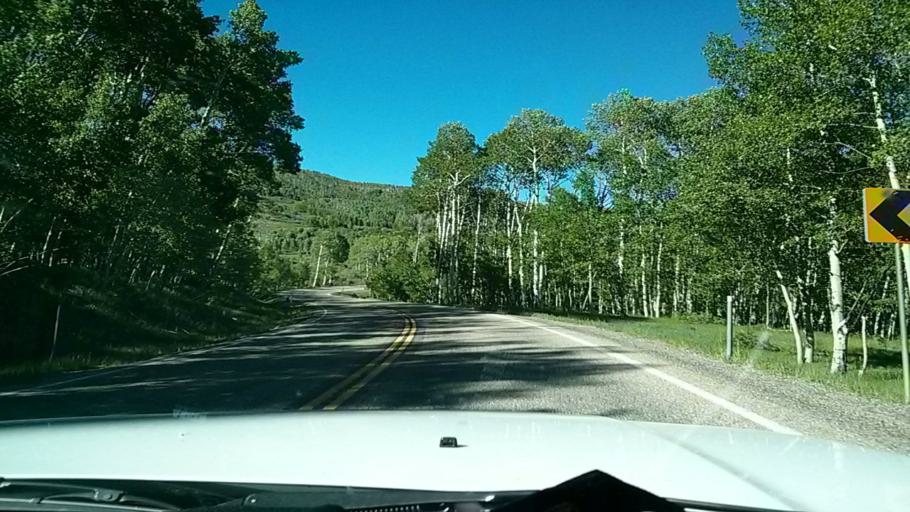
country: US
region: Utah
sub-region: Wayne County
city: Loa
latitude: 38.0236
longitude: -111.3509
